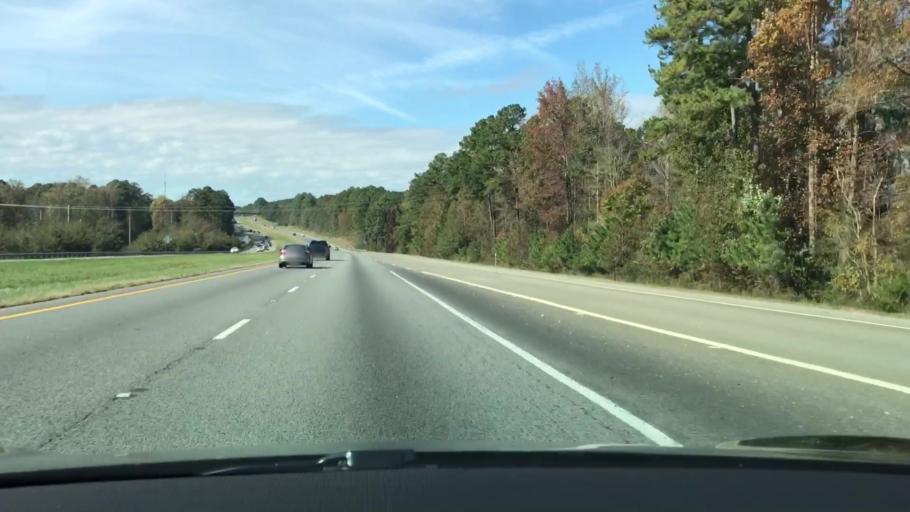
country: US
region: Georgia
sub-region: Walton County
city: Social Circle
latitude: 33.6105
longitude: -83.7050
